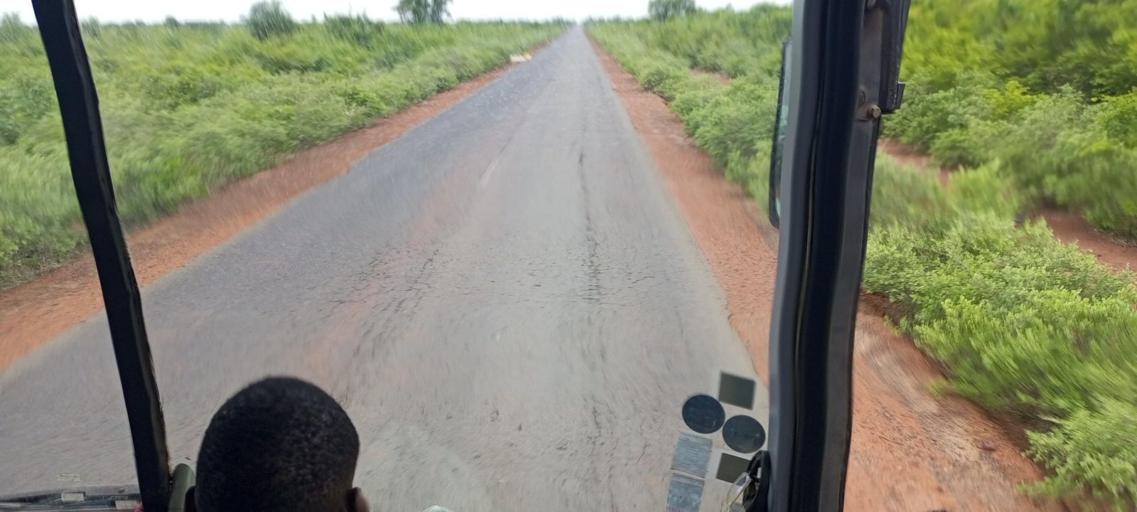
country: ML
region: Sikasso
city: Koutiala
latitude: 12.5537
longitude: -5.5870
